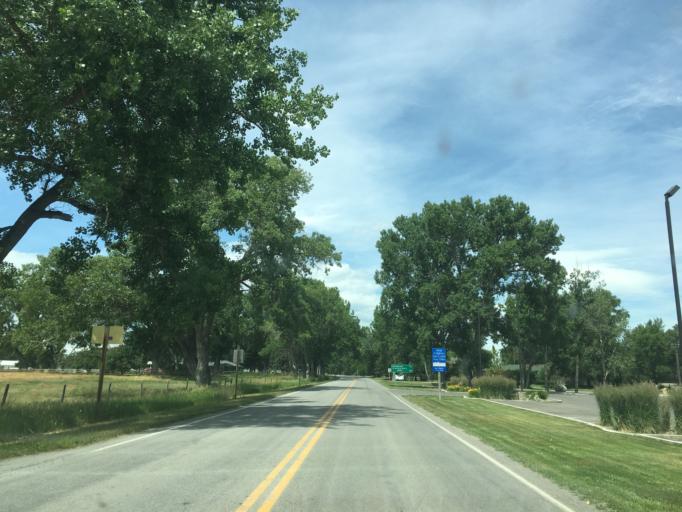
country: US
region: Montana
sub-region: Teton County
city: Choteau
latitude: 47.8217
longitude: -112.1905
